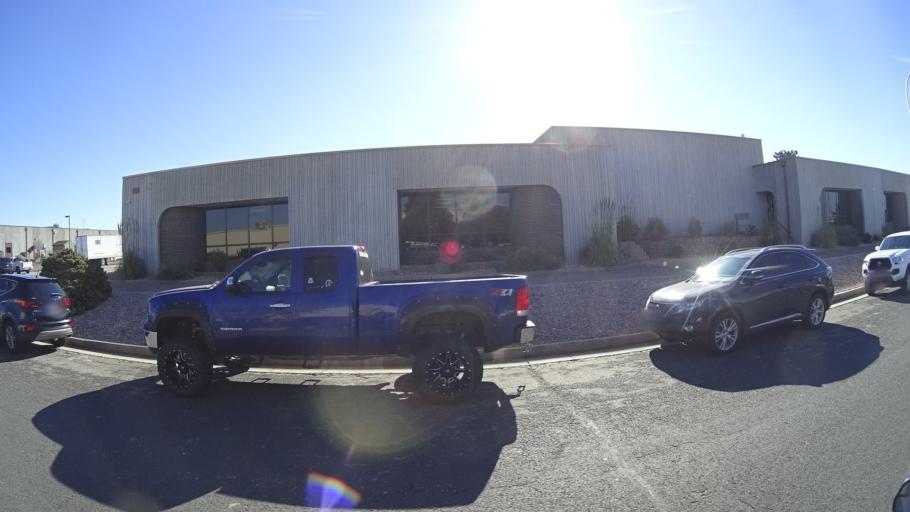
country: US
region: Colorado
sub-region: El Paso County
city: Cimarron Hills
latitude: 38.8129
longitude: -104.7254
